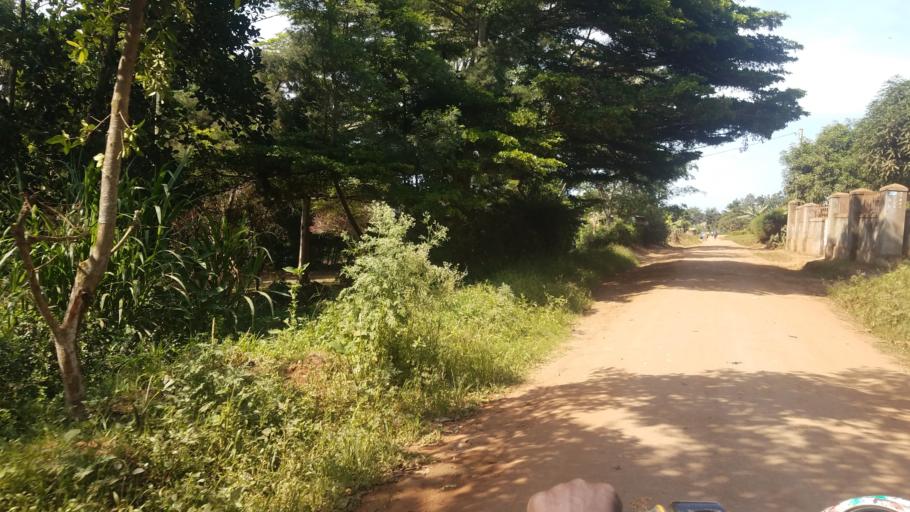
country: UG
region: Central Region
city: Masaka
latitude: -0.3322
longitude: 31.7094
